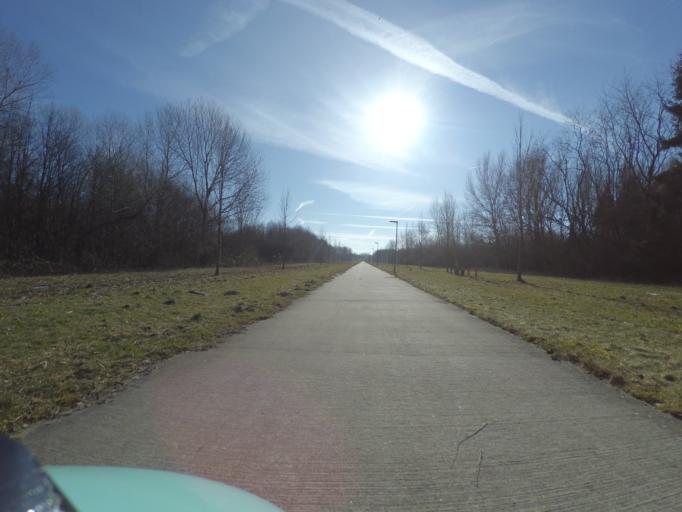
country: NL
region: Flevoland
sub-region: Gemeente Almere
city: Almere Stad
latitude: 52.3849
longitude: 5.1748
